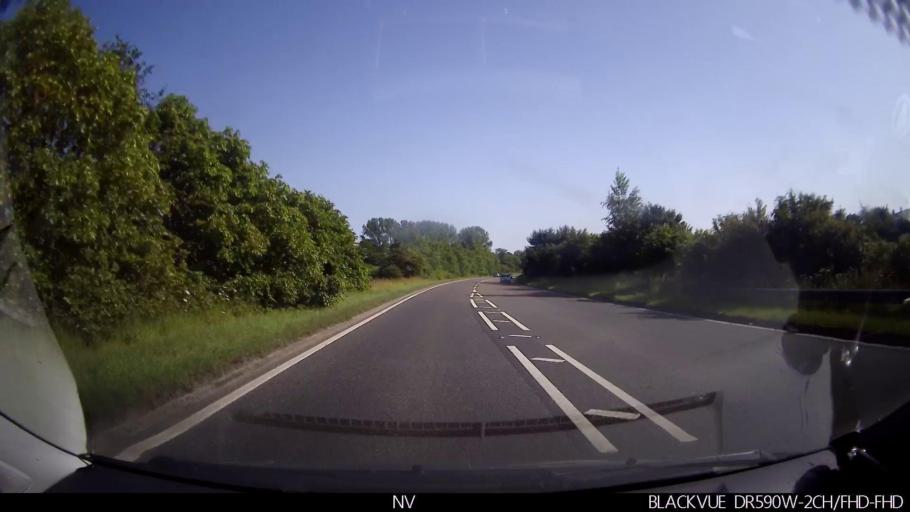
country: GB
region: England
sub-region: North Yorkshire
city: Scarborough
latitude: 54.2448
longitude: -0.4151
